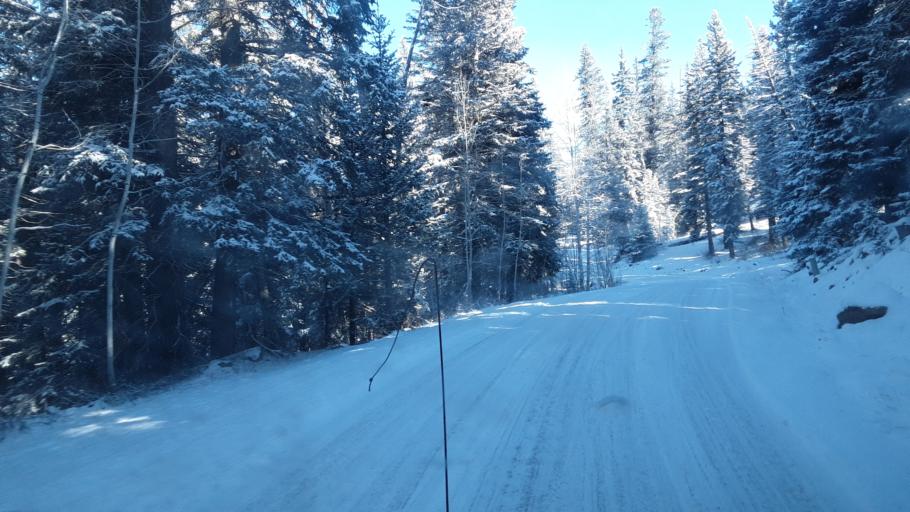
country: US
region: Colorado
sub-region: La Plata County
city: Bayfield
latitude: 37.4407
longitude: -107.6800
